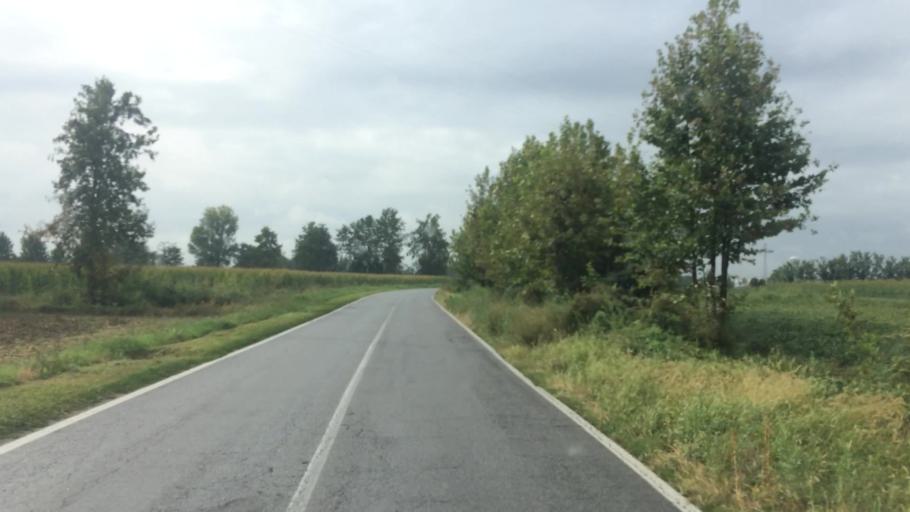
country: IT
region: Lombardy
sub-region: Provincia di Brescia
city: Longhena
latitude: 45.4267
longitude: 10.0649
